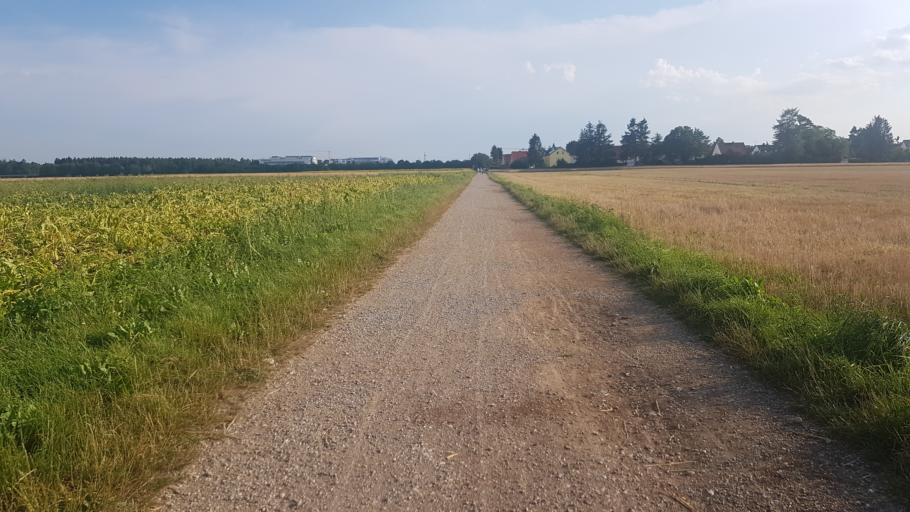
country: DE
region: Bavaria
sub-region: Upper Bavaria
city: Pasing
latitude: 48.1323
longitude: 11.4545
